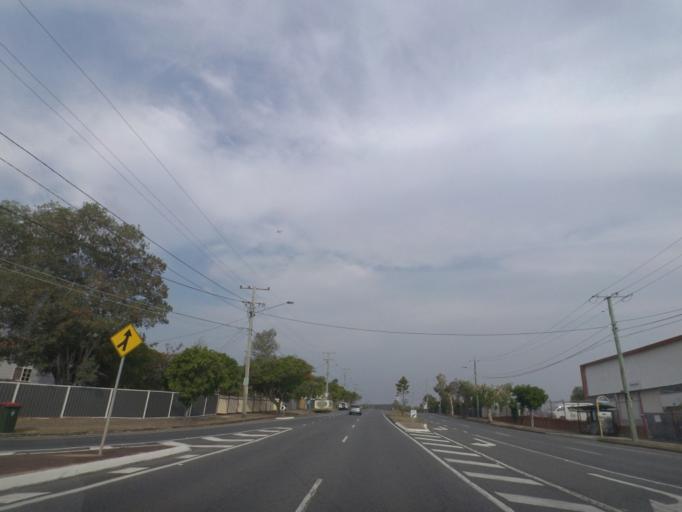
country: AU
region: Queensland
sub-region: Brisbane
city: Tarragindi
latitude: -27.5436
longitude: 153.0220
